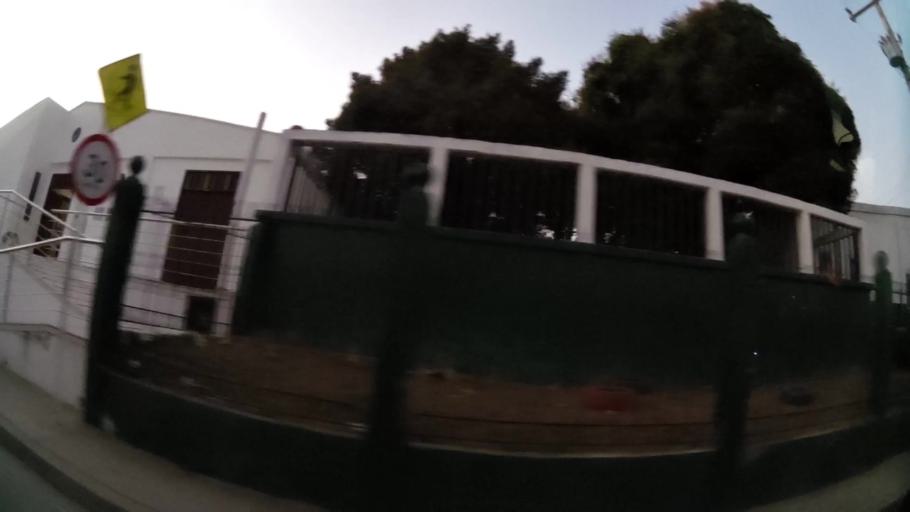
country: CO
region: Bolivar
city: Cartagena
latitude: 10.3892
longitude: -75.4930
